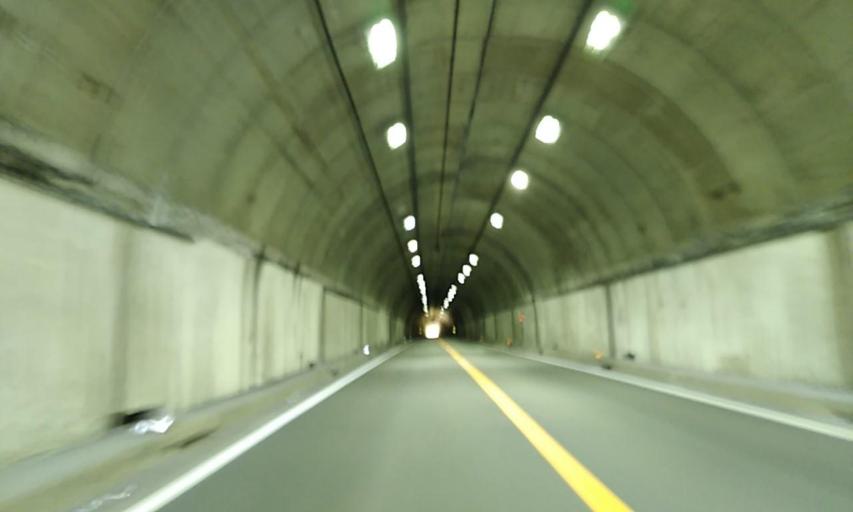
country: JP
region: Wakayama
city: Gobo
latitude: 33.9901
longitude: 135.1773
